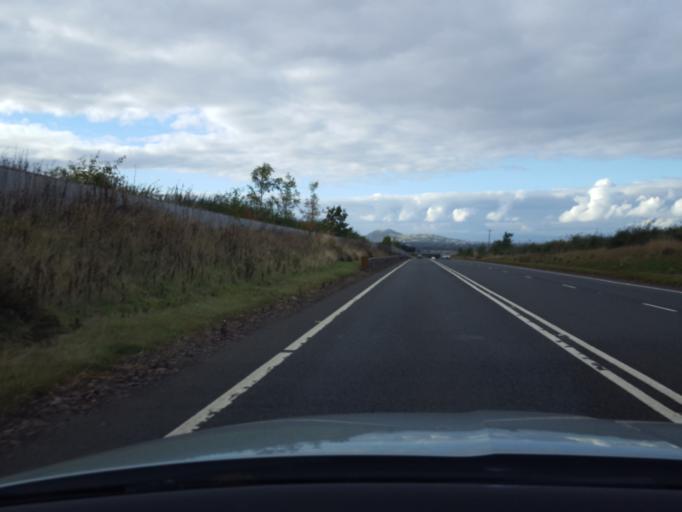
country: GB
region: Scotland
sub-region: Midlothian
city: Dalkeith
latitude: 55.8987
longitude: -3.0168
